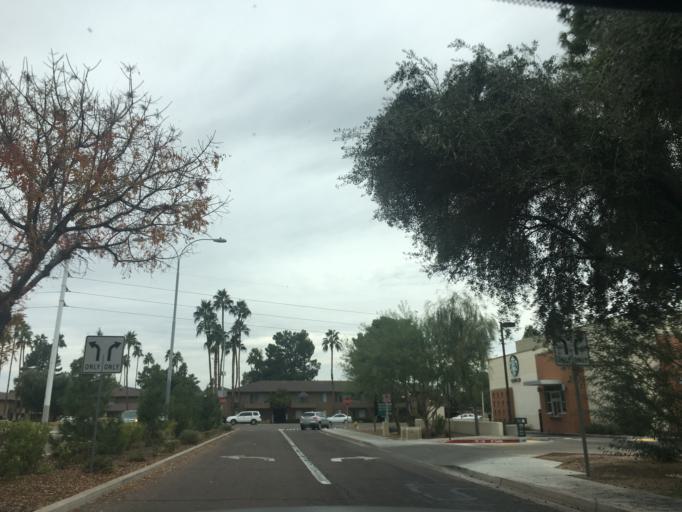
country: US
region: Arizona
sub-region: Maricopa County
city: Tempe Junction
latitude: 33.3821
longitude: -111.9260
